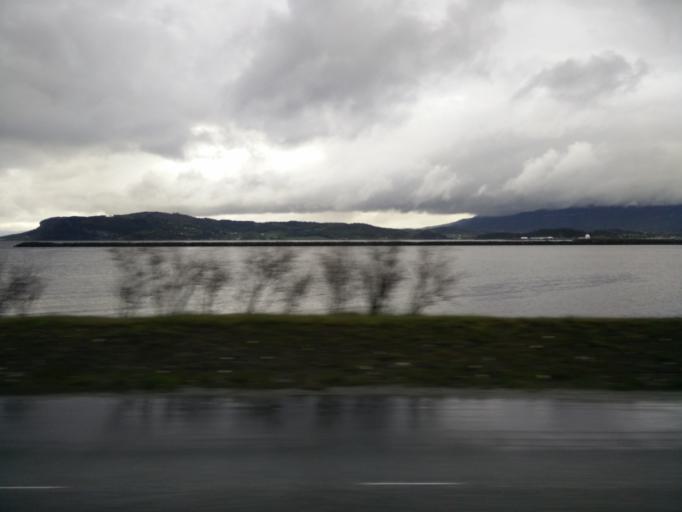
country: NO
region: Nord-Trondelag
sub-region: Stjordal
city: Stjordal
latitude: 63.4449
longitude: 10.8799
